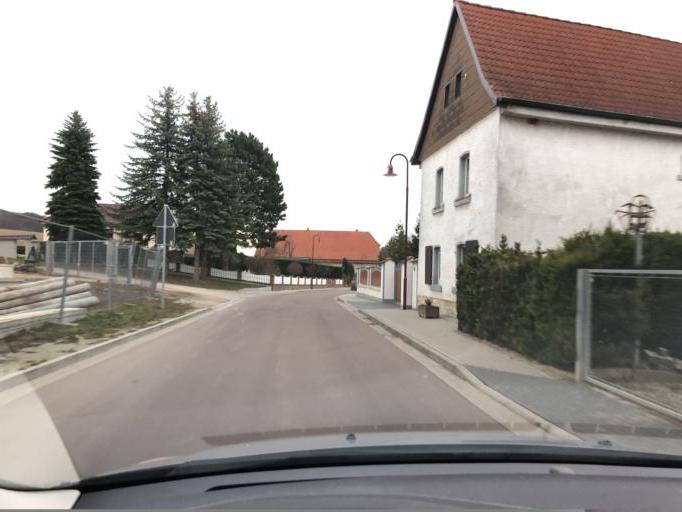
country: DE
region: Saxony-Anhalt
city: Bad Bibra
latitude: 51.1768
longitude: 11.5994
